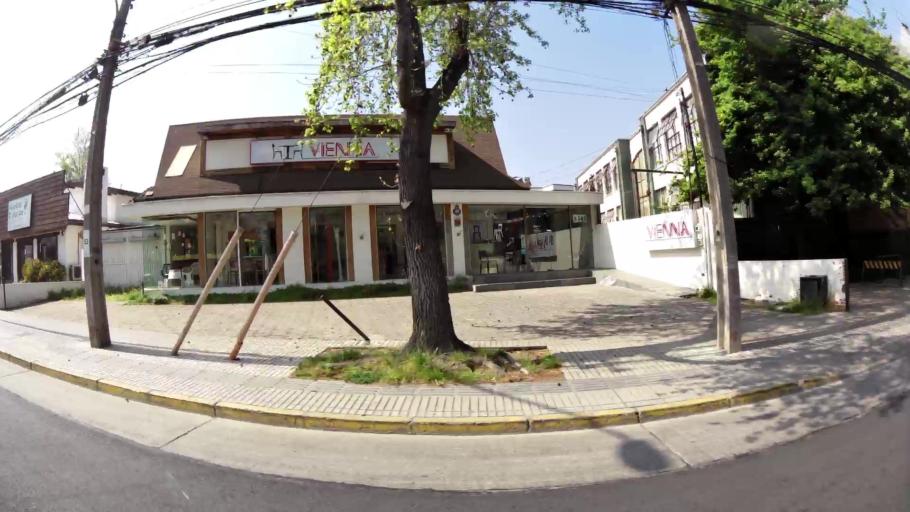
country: CL
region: Santiago Metropolitan
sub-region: Provincia de Santiago
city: Villa Presidente Frei, Nunoa, Santiago, Chile
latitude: -33.3838
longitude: -70.5733
